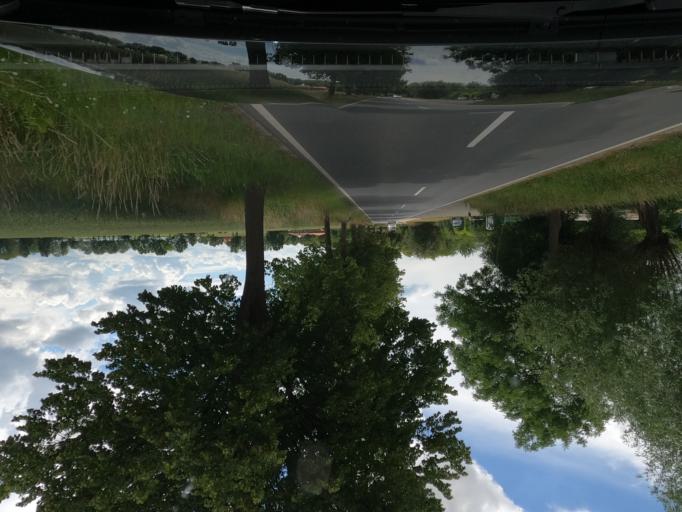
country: DE
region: Lower Saxony
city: Hohenhameln
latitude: 52.2533
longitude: 10.0193
